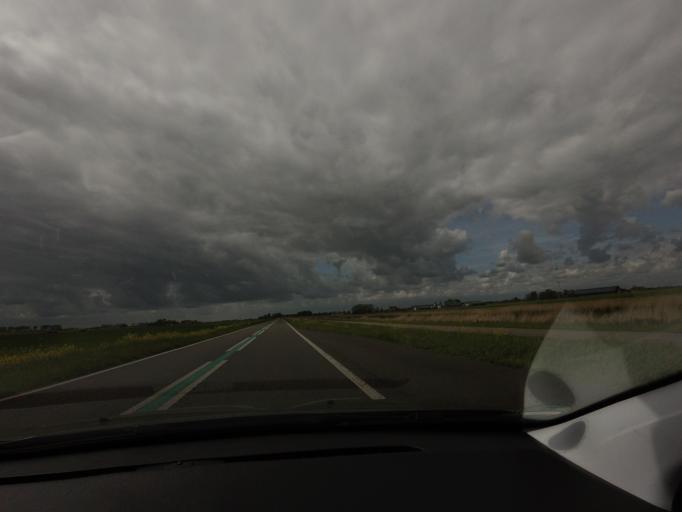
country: NL
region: Friesland
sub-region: Sudwest Fryslan
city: Koudum
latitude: 52.9385
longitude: 5.4438
